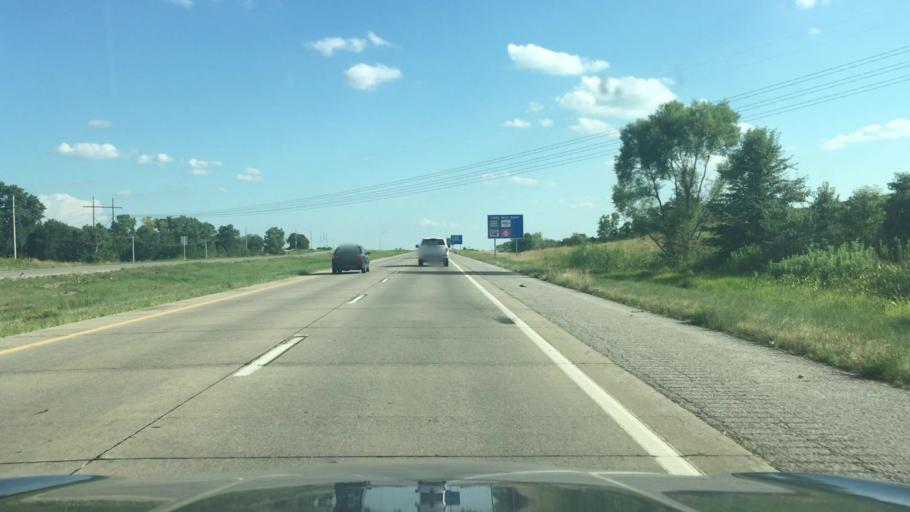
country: US
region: Missouri
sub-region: Jackson County
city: Greenwood
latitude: 38.8633
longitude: -94.3754
